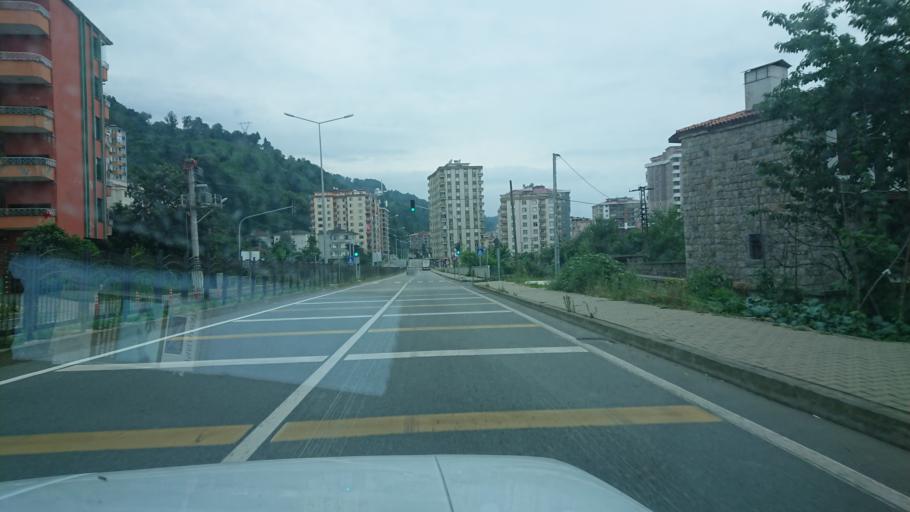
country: TR
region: Rize
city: Gundogdu
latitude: 41.0354
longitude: 40.5647
